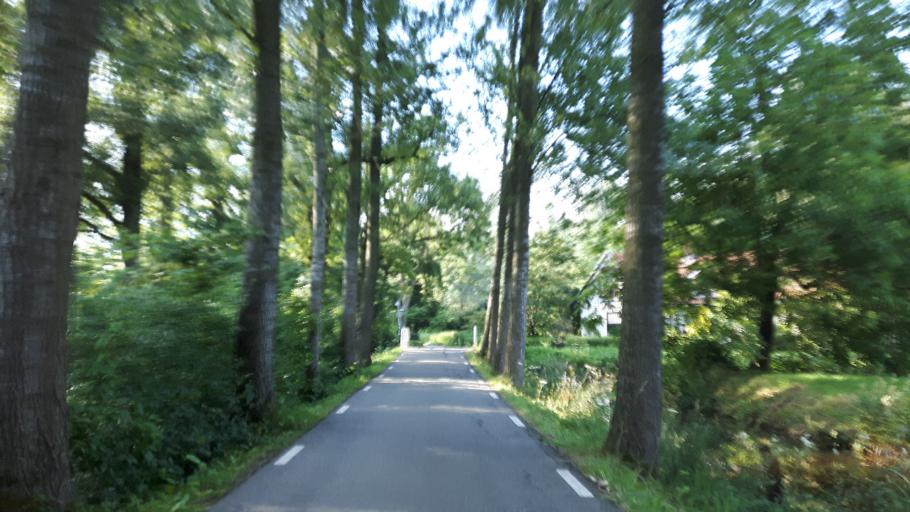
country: NL
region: Utrecht
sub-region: Gemeente Woerden
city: Woerden
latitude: 52.0633
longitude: 4.8982
